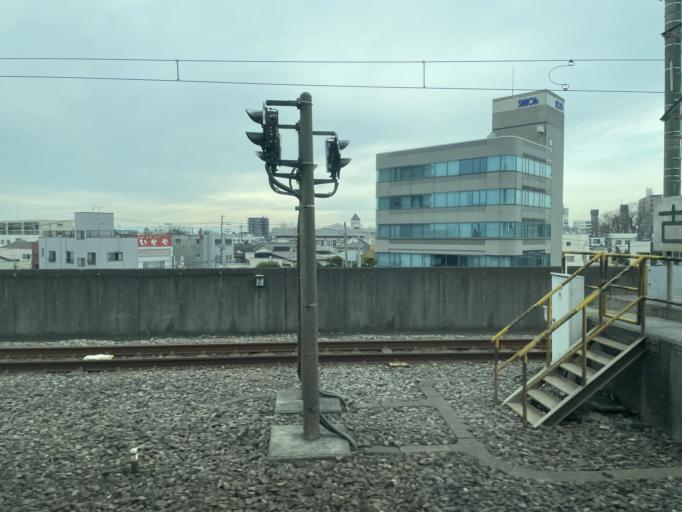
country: JP
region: Ibaraki
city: Koga
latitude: 36.1929
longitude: 139.7100
